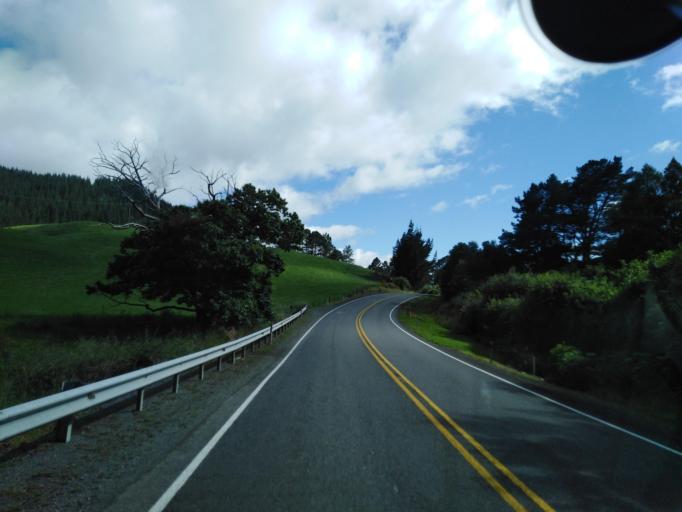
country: NZ
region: Nelson
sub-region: Nelson City
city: Nelson
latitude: -41.2884
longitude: 173.5714
